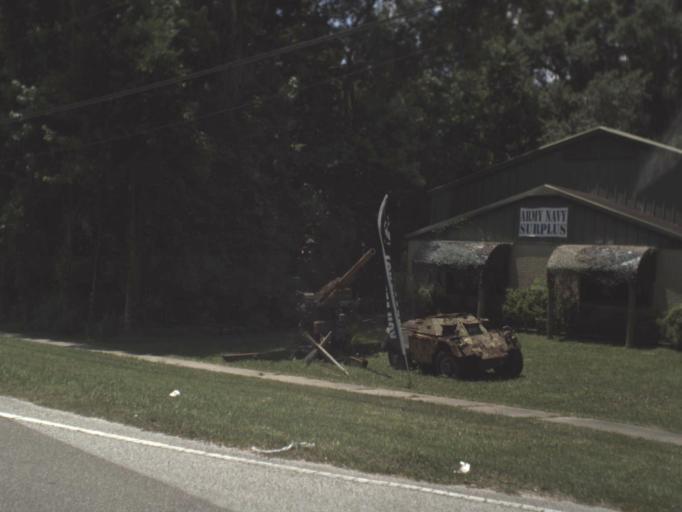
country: US
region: Florida
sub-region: Hernando County
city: Brooksville
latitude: 28.5489
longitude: -82.3813
